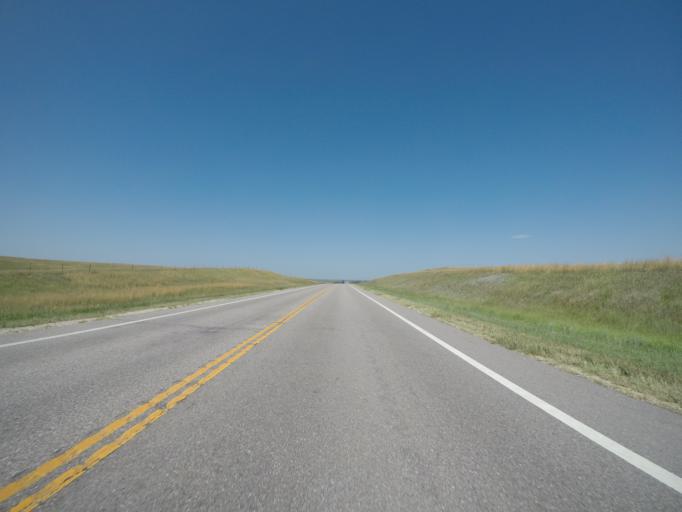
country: US
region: Kansas
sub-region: Cloud County
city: Concordia
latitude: 39.3648
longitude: -97.7317
